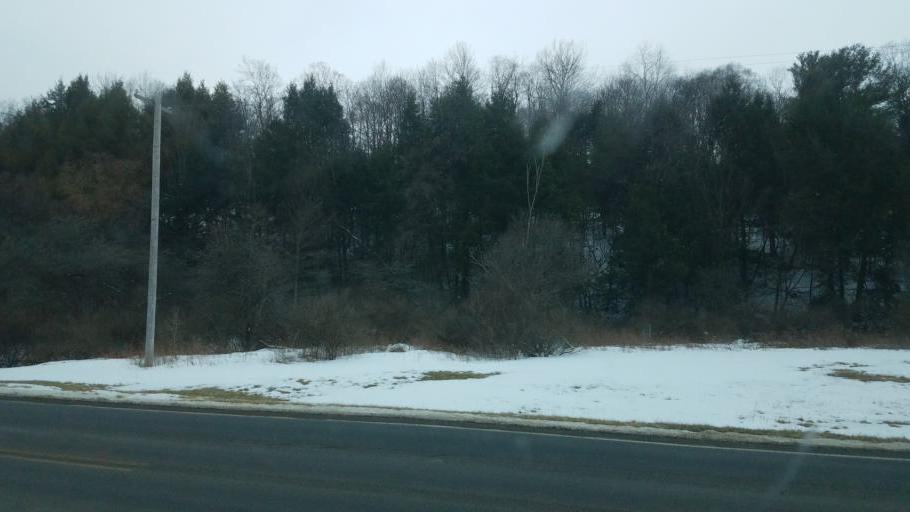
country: US
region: New York
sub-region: Allegany County
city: Andover
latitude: 42.0327
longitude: -77.7531
